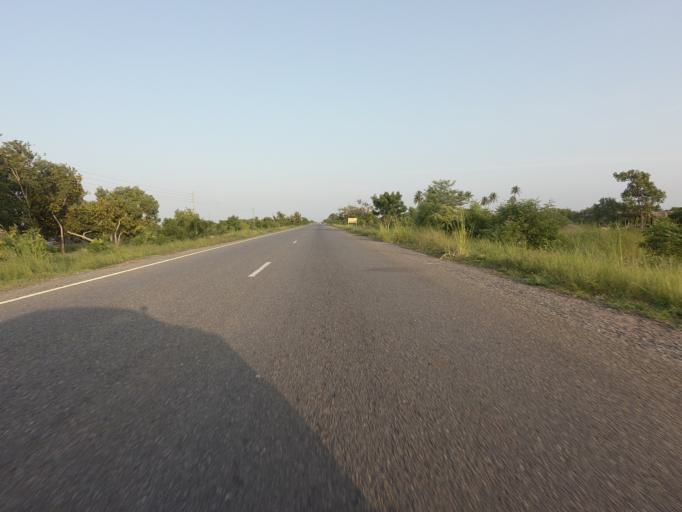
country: GH
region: Volta
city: Anloga
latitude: 5.8912
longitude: 0.7188
